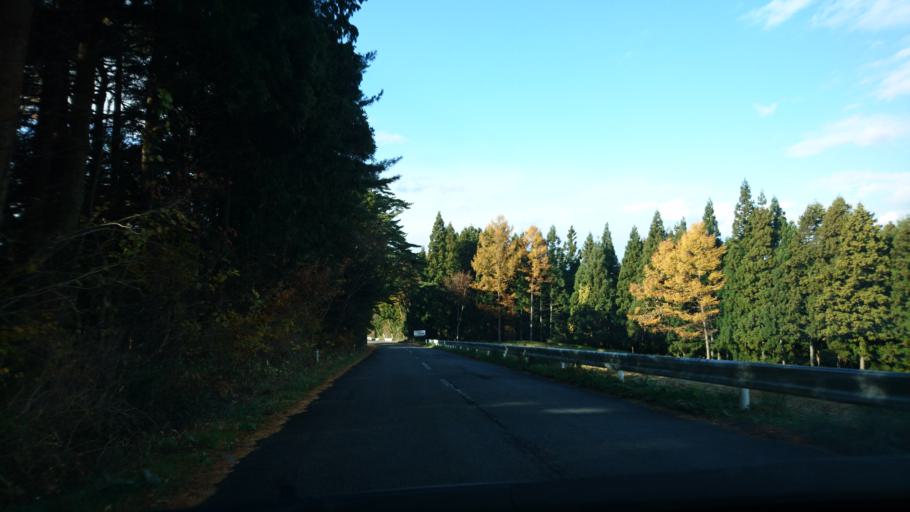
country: JP
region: Iwate
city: Mizusawa
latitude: 39.0298
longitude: 141.1633
